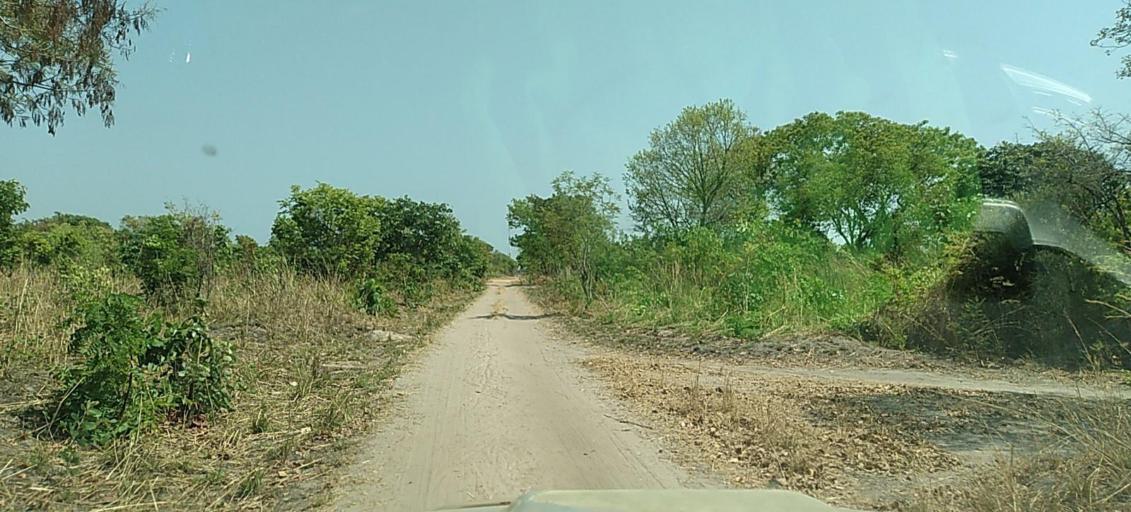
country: ZM
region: North-Western
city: Kalengwa
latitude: -13.2344
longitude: 24.7521
